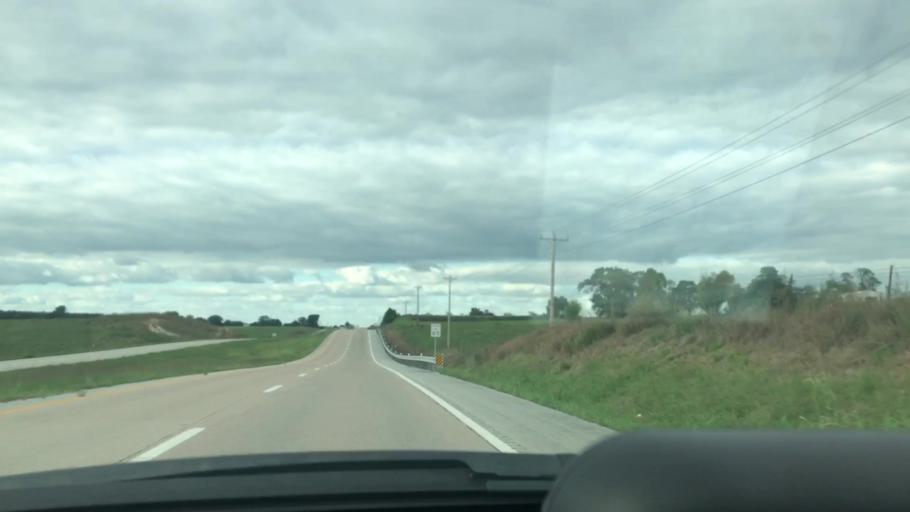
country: US
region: Missouri
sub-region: Benton County
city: Lincoln
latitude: 38.3207
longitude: -93.3421
